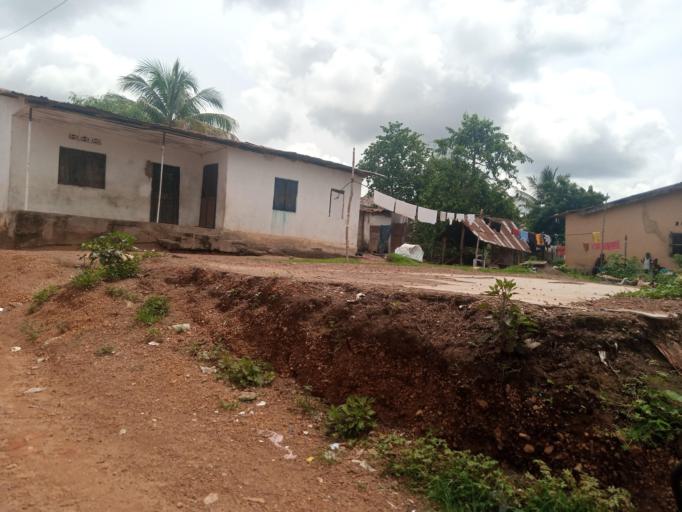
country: SL
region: Southern Province
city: Bo
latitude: 7.9544
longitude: -11.7175
